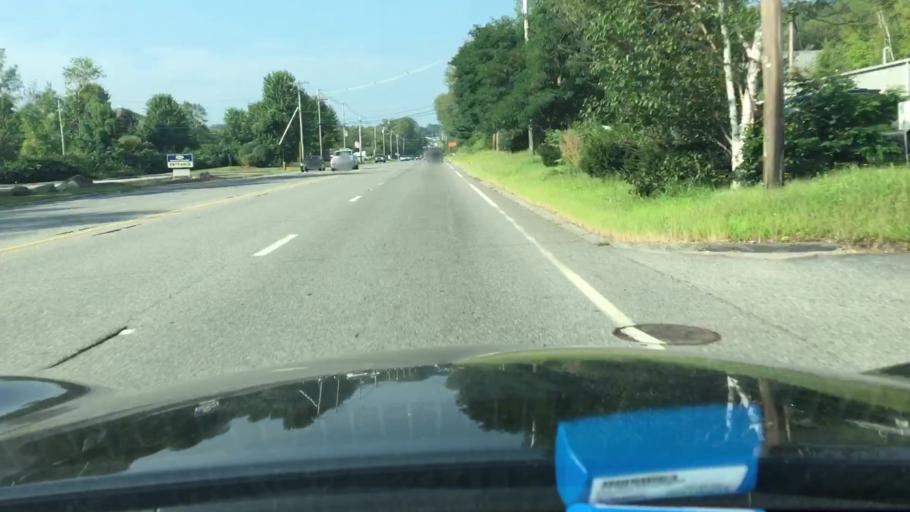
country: US
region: Massachusetts
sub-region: Worcester County
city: Shrewsbury
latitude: 42.2773
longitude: -71.6762
